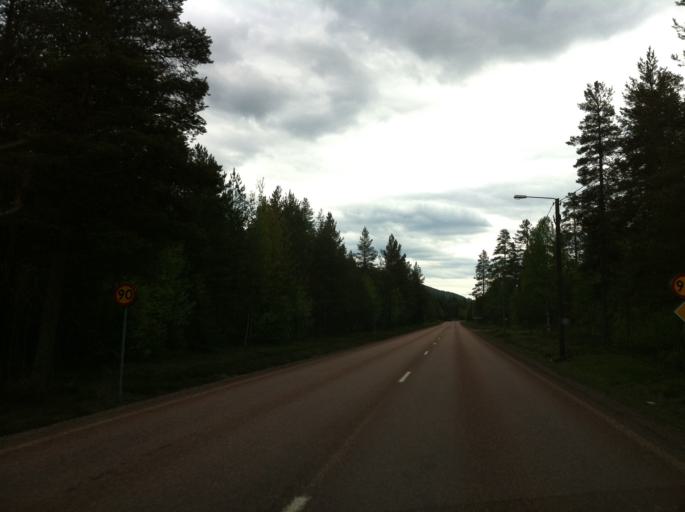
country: SE
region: Dalarna
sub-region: Malung-Saelens kommun
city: Malung
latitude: 61.0734
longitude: 13.3290
